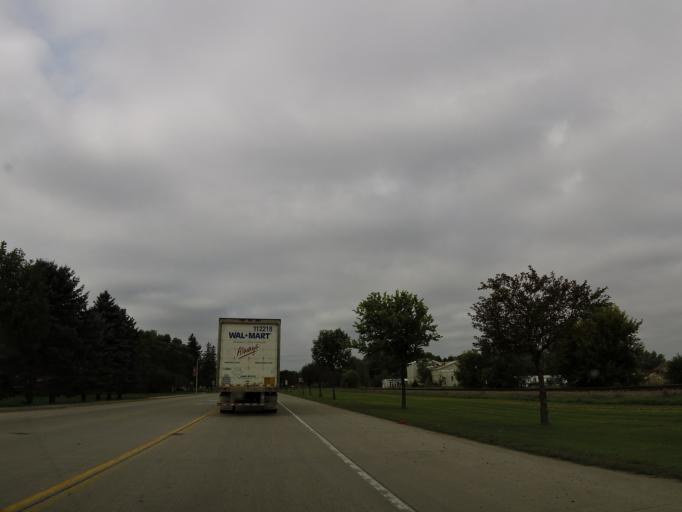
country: US
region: Minnesota
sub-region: Renville County
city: Olivia
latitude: 44.7762
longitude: -94.9766
